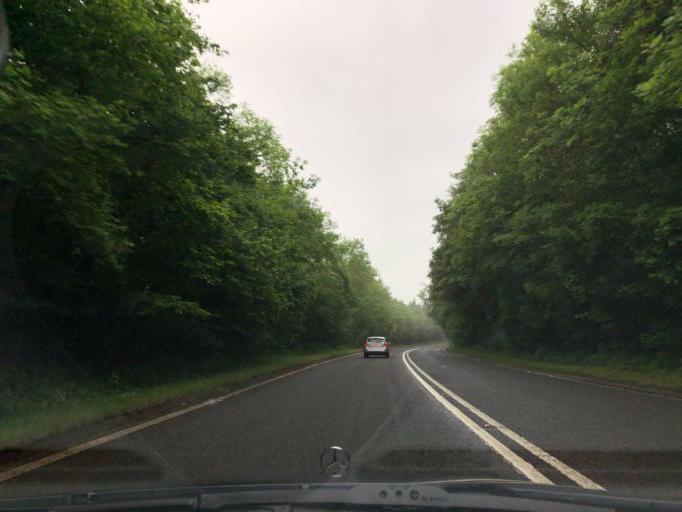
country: GB
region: England
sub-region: Warwickshire
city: Harbury
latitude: 52.2092
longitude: -1.5026
